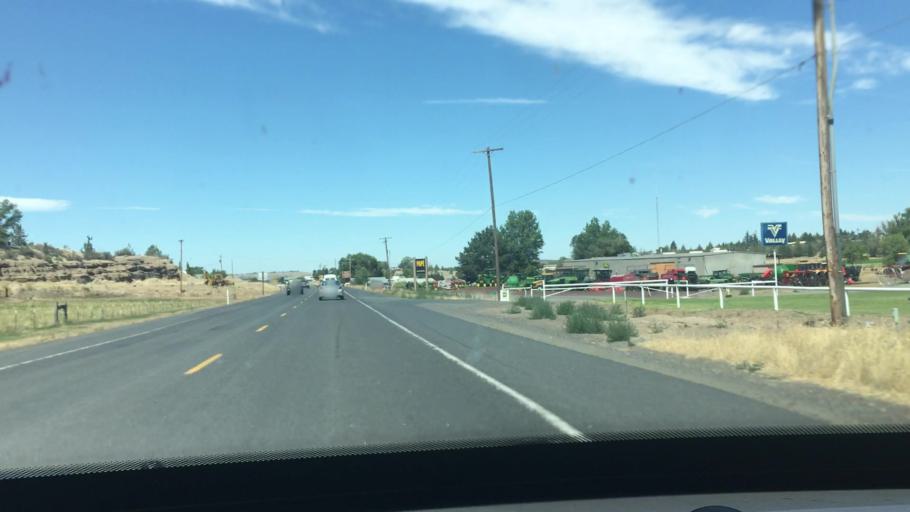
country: US
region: Oregon
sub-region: Jefferson County
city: Madras
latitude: 44.6004
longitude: -121.1427
